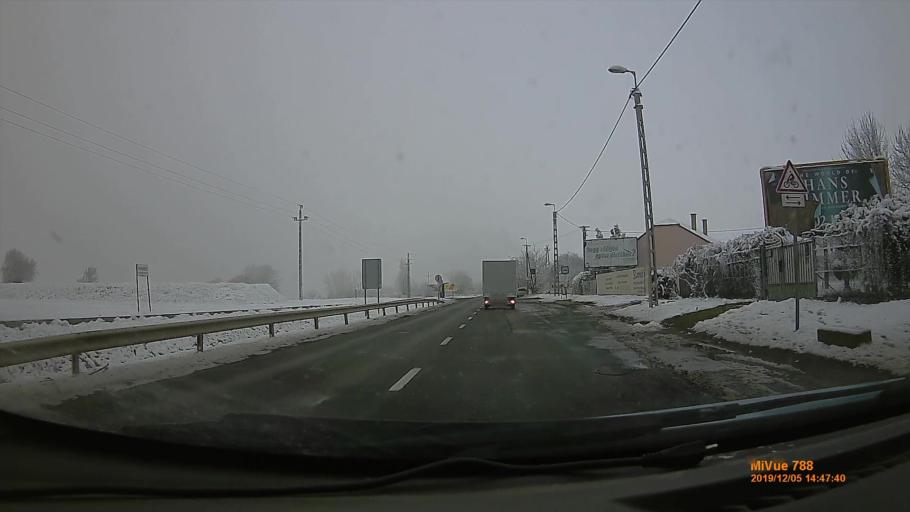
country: HU
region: Szabolcs-Szatmar-Bereg
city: Nyiregyhaza
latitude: 47.9709
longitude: 21.6935
